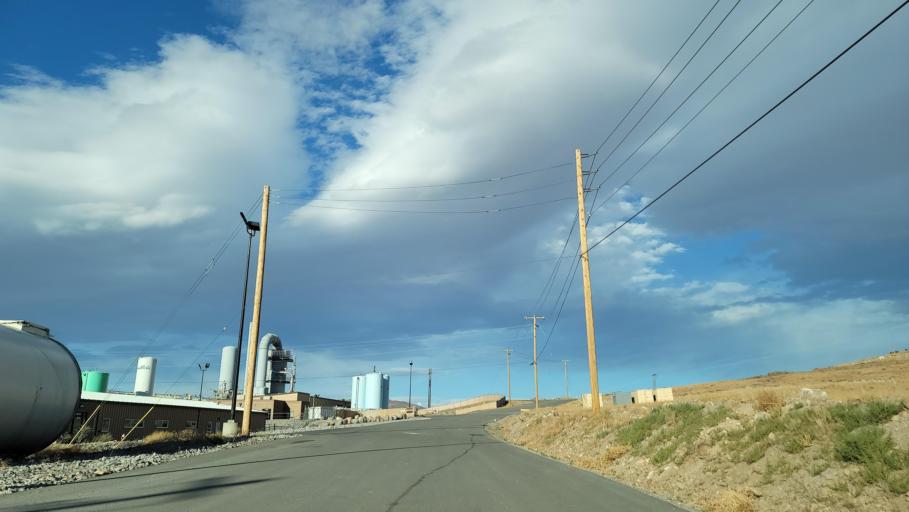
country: US
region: Nevada
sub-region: Washoe County
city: Spanish Springs
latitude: 39.5528
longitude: -119.5206
